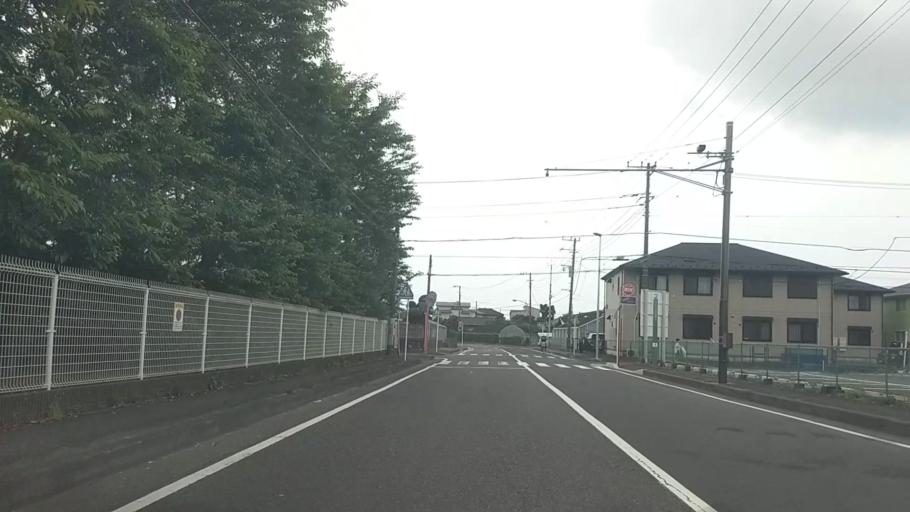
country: JP
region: Kanagawa
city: Fujisawa
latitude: 35.3403
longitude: 139.4727
